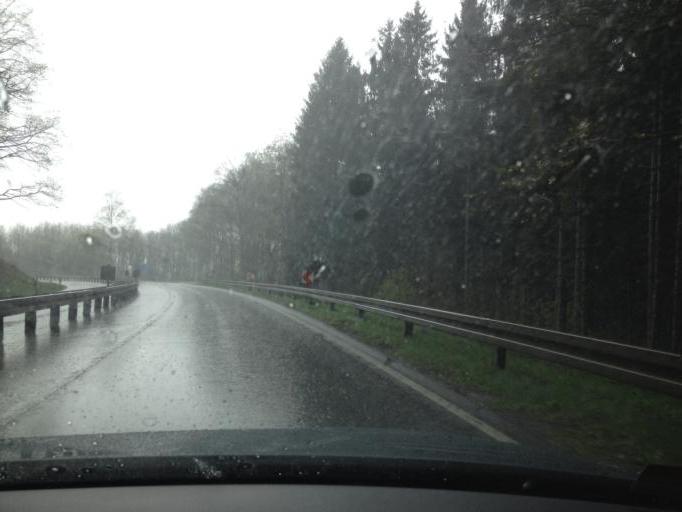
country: DE
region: Saarland
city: Ottweiler
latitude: 49.3917
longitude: 7.1531
